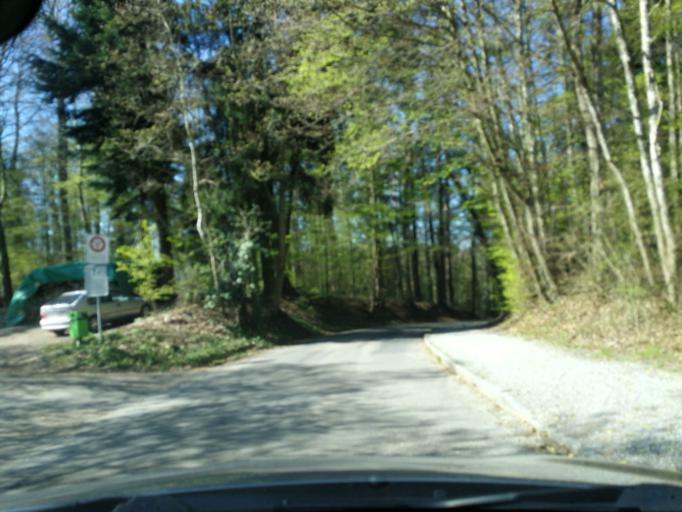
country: CH
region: Zurich
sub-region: Bezirk Meilen
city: Uetikon / Grossdorf
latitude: 47.2838
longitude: 8.6769
